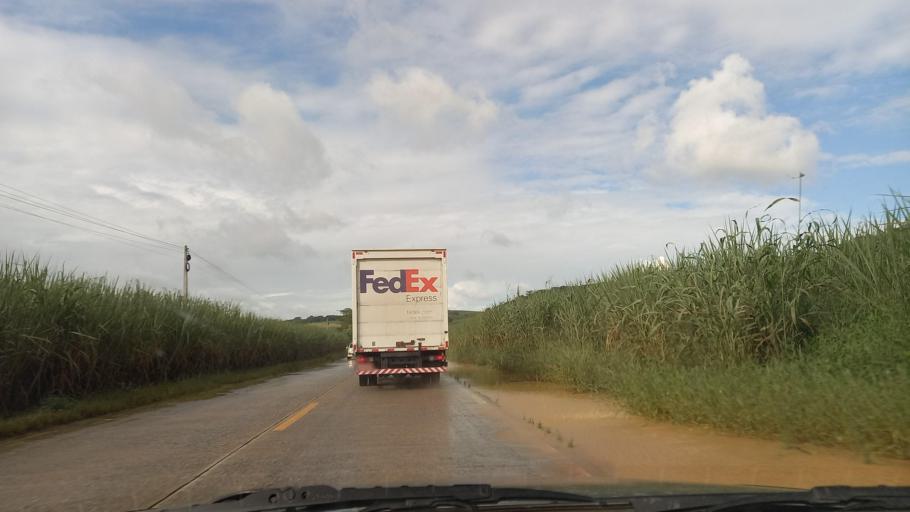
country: BR
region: Pernambuco
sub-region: Catende
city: Catende
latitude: -8.6936
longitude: -35.6837
